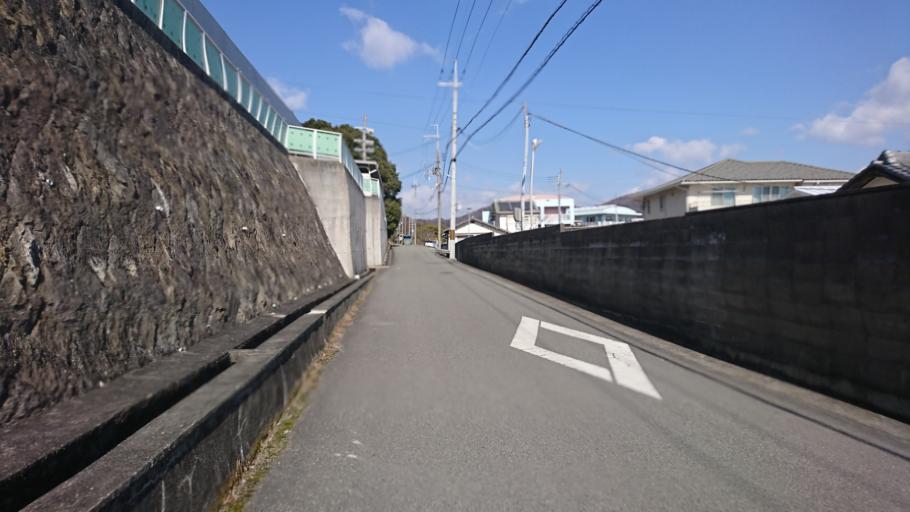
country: JP
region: Hyogo
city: Kakogawacho-honmachi
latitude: 34.8148
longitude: 134.8035
